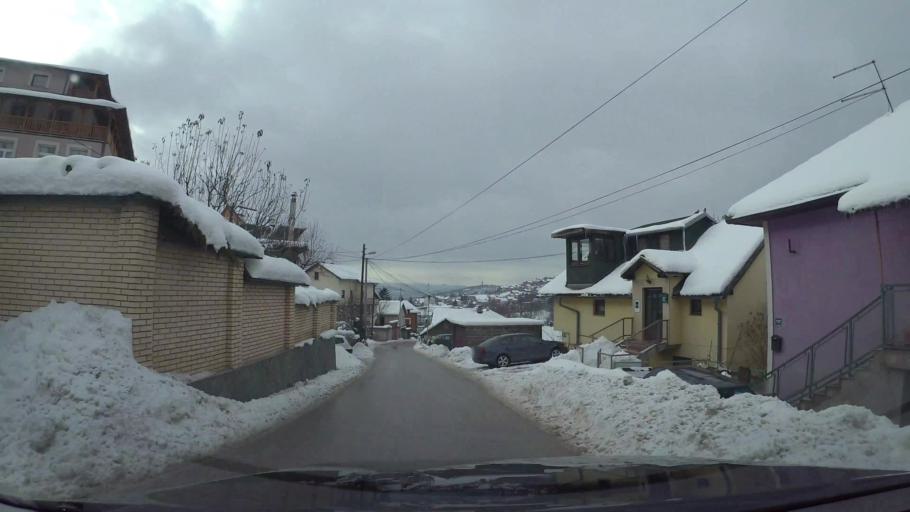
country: BA
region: Federation of Bosnia and Herzegovina
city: Kobilja Glava
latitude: 43.8734
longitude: 18.4410
